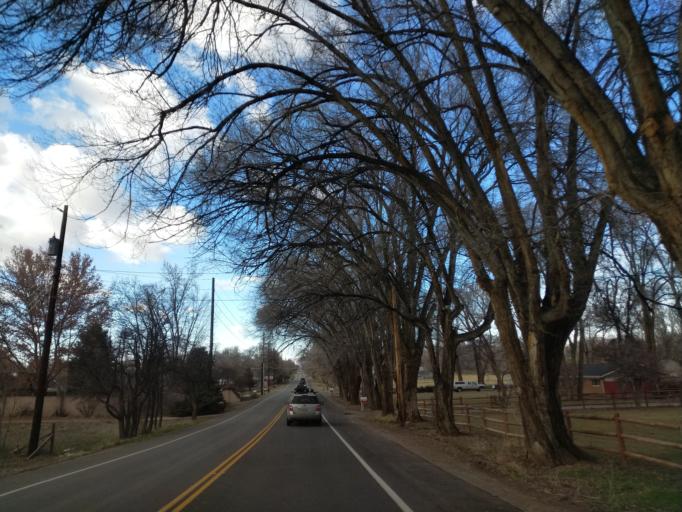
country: US
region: Colorado
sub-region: Mesa County
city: Grand Junction
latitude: 39.0979
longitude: -108.5708
